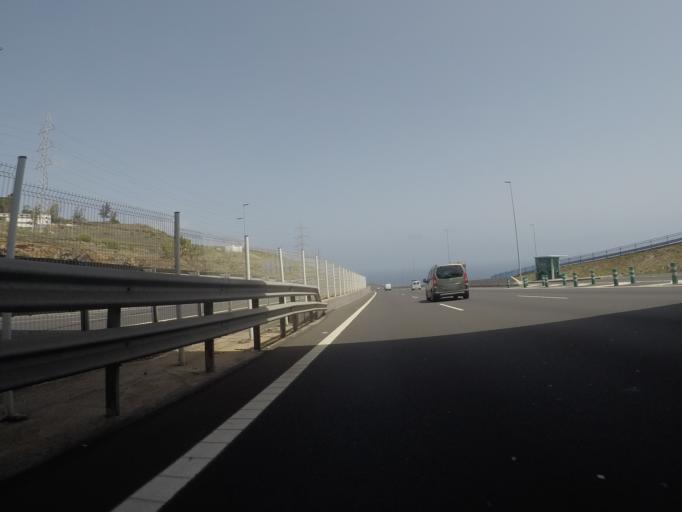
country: ES
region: Canary Islands
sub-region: Provincia de Santa Cruz de Tenerife
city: Santa Cruz de Tenerife
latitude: 28.4321
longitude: -16.2914
